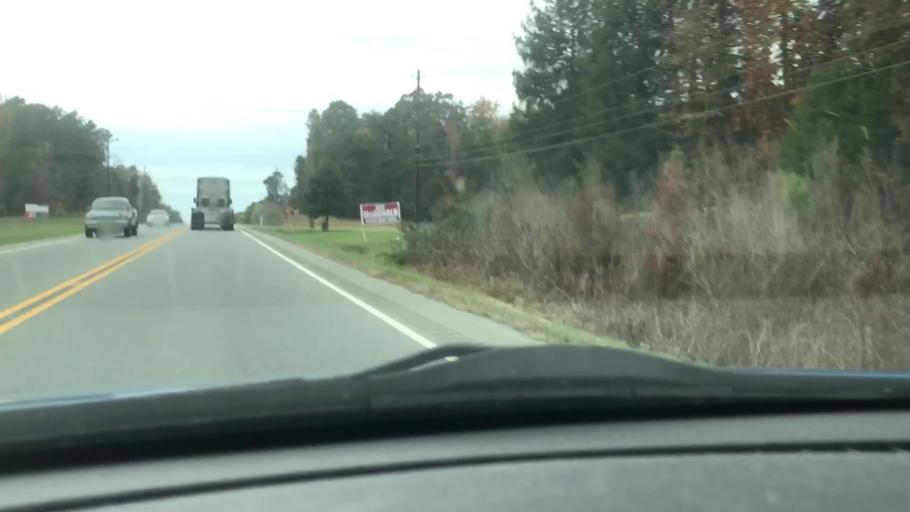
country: US
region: North Carolina
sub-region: Davidson County
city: Thomasville
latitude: 35.7952
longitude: -80.1469
